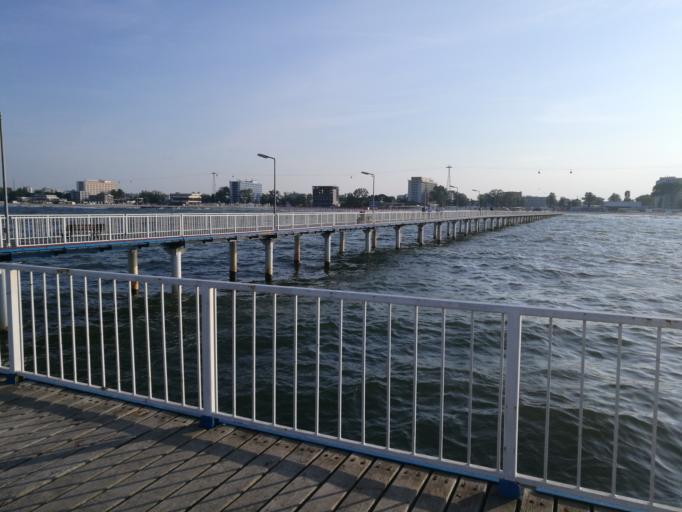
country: RO
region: Constanta
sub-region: Municipiul Constanta
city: Palazu Mare
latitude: 44.2320
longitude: 28.6341
